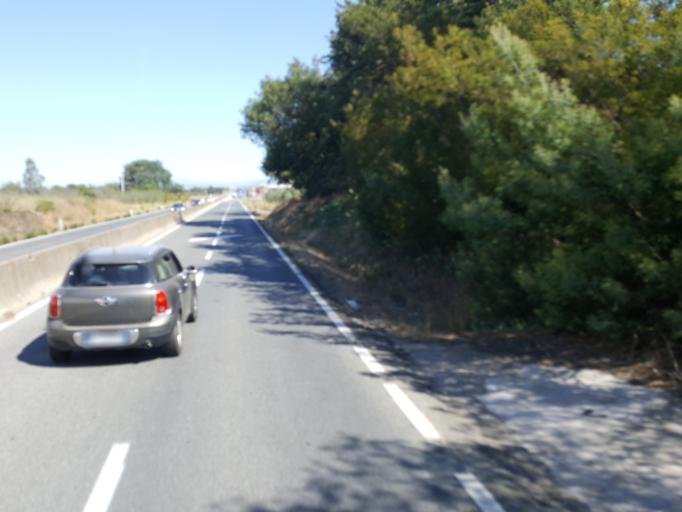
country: IT
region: Tuscany
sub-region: Provincia di Grosseto
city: Grosseto
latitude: 42.6716
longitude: 11.1420
